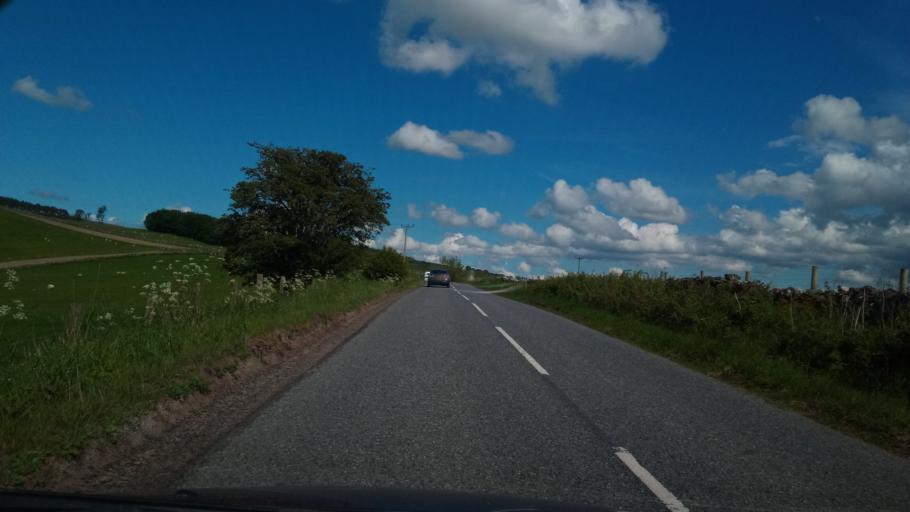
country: GB
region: Scotland
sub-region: The Scottish Borders
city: Jedburgh
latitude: 55.3899
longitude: -2.6161
